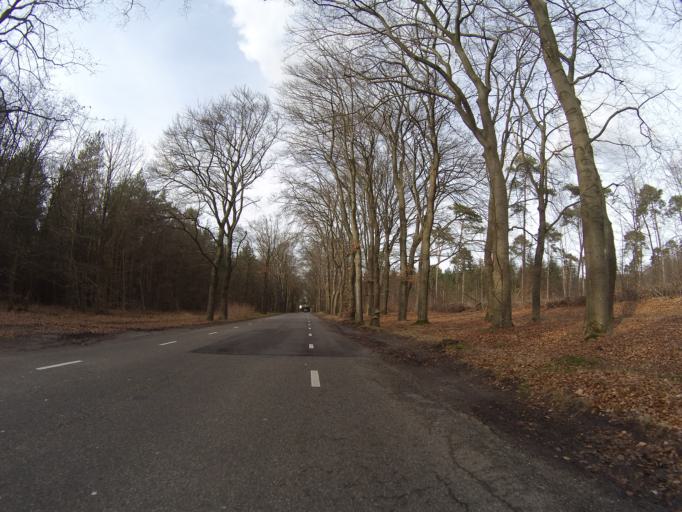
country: NL
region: Utrecht
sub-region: Gemeente Utrechtse Heuvelrug
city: Driebergen-Rijsenburg
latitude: 52.0743
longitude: 5.3202
